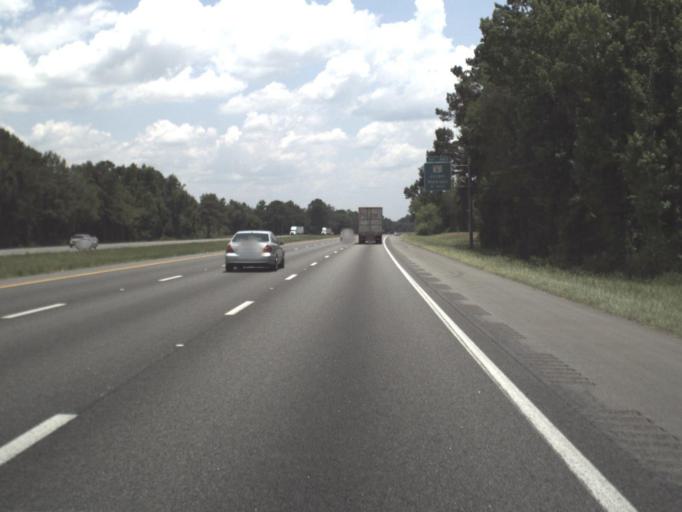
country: US
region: Florida
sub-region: Hamilton County
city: Jasper
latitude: 30.5461
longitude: -83.0768
